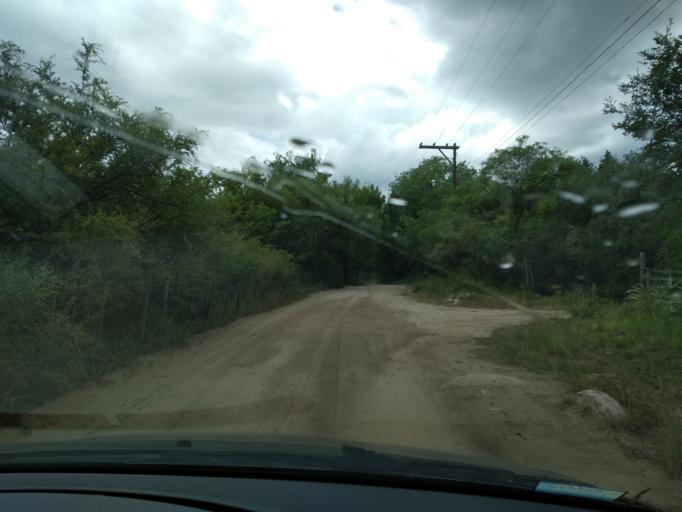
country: AR
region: Cordoba
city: Villa Las Rosas
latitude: -31.9456
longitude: -65.0358
